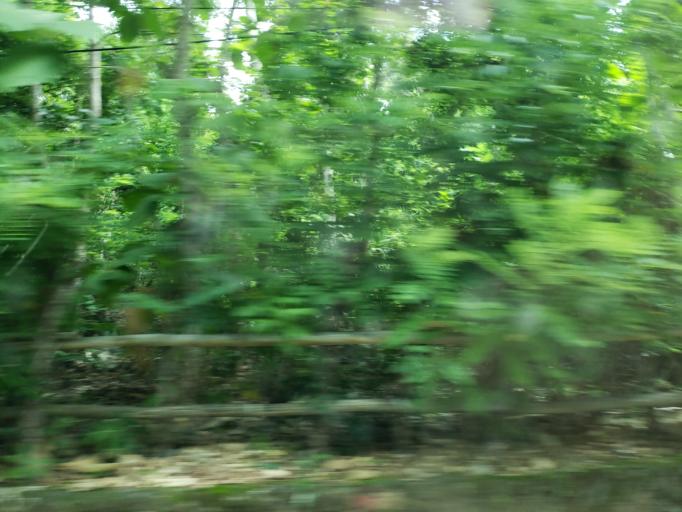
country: ID
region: Bali
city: Pecatu
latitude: -8.8405
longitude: 115.1259
